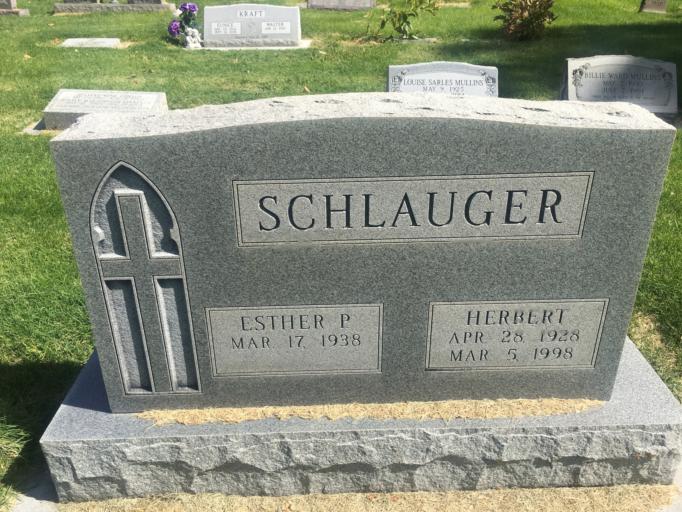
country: US
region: Colorado
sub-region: Mesa County
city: Orchard Mesa
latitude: 39.0437
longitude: -108.5683
